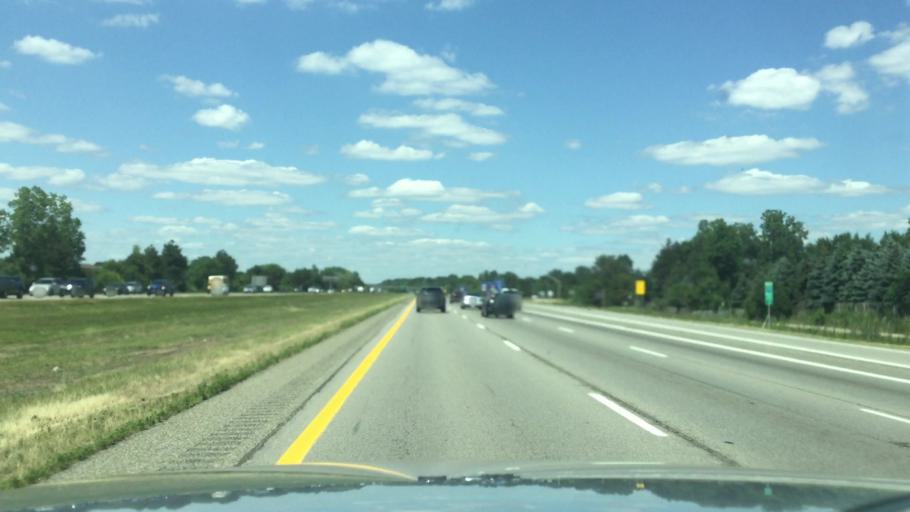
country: US
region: Michigan
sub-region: Wayne County
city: Canton
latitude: 42.2964
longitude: -83.4432
